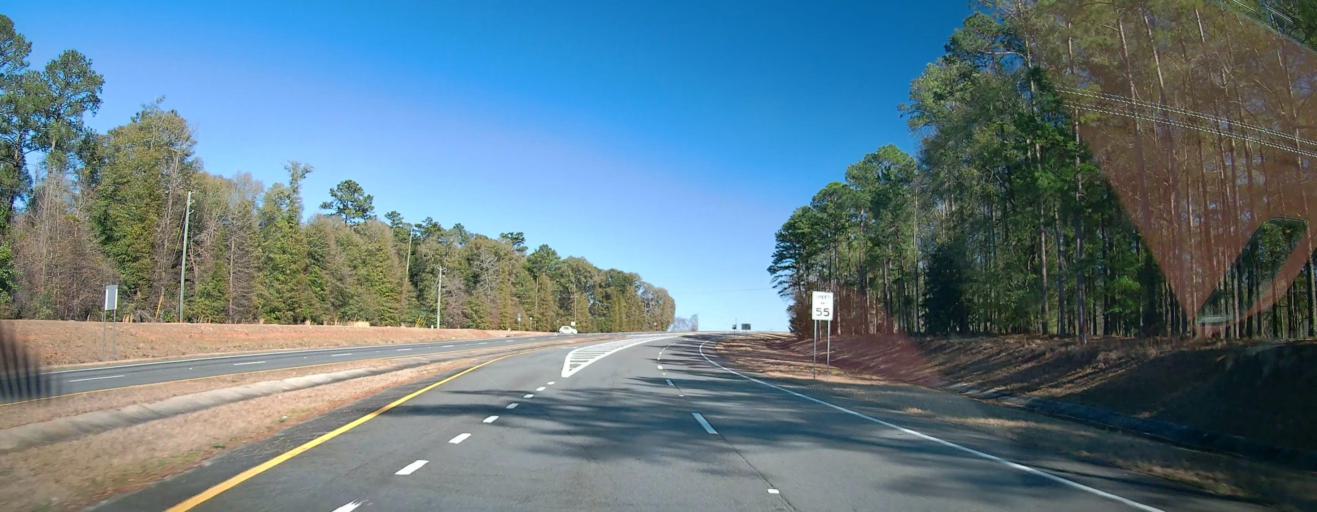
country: US
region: Georgia
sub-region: Sumter County
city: Americus
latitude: 32.1145
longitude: -84.2520
